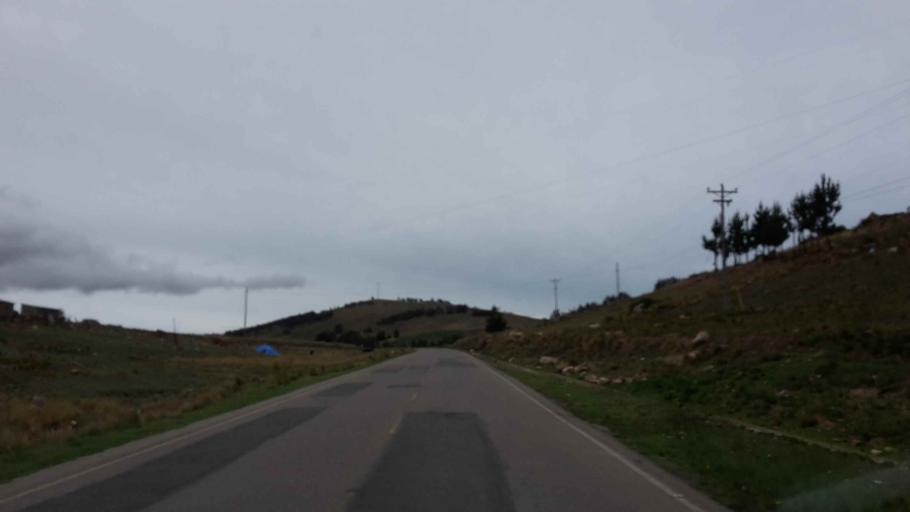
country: BO
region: Cochabamba
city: Arani
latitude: -17.4841
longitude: -65.6156
